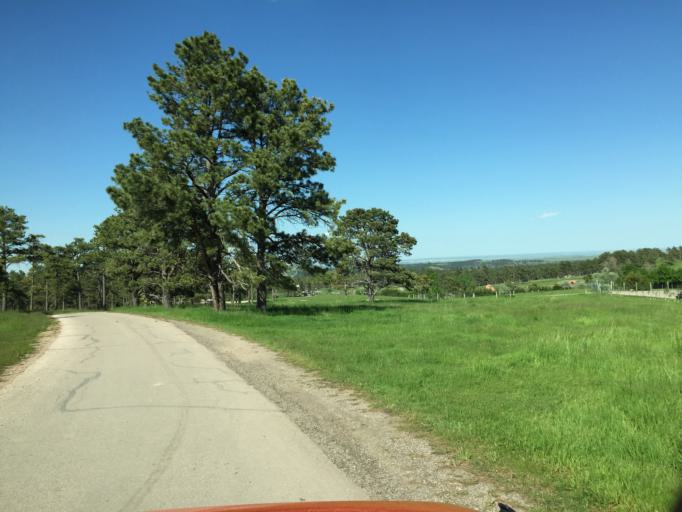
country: US
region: South Dakota
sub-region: Pennington County
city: Colonial Pine Hills
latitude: 43.9766
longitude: -103.3029
